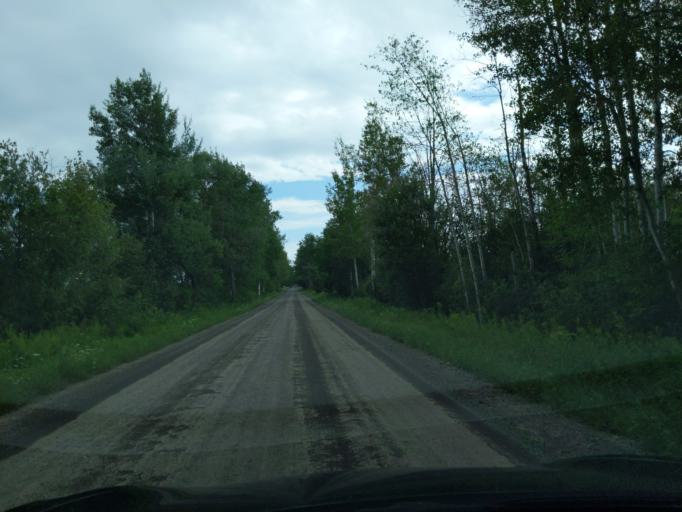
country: US
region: Michigan
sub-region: Clare County
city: Harrison
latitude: 43.9854
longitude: -84.9983
